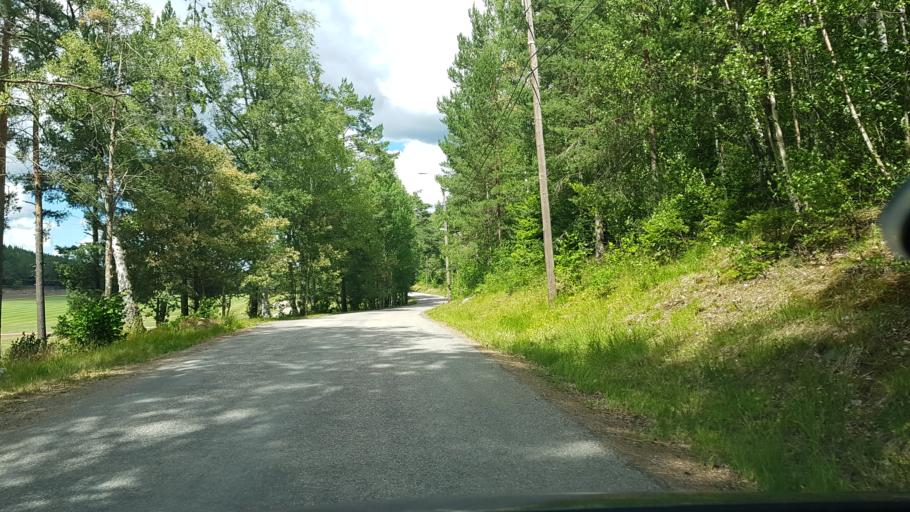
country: SE
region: Stockholm
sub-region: Upplands-Bro Kommun
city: Kungsaengen
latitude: 59.4856
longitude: 17.8035
